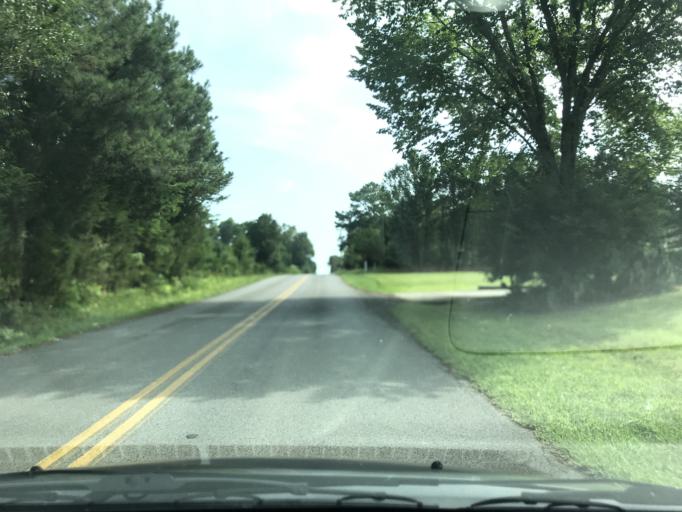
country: US
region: Tennessee
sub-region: Hamilton County
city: Apison
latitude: 35.0710
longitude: -84.9782
